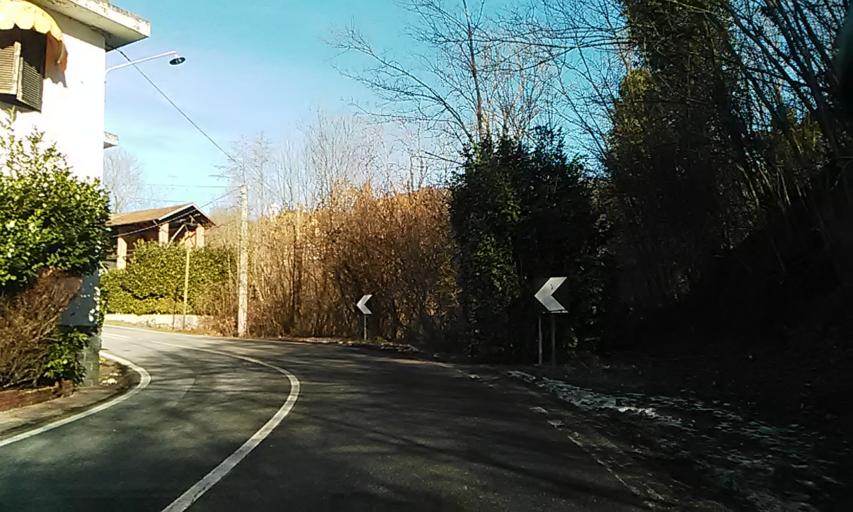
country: IT
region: Piedmont
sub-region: Provincia di Vercelli
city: Cellio
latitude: 45.7378
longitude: 8.3043
